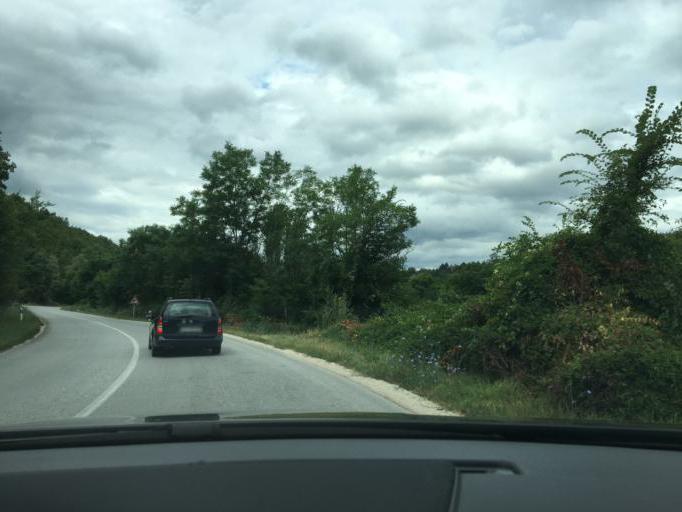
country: MK
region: Kratovo
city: Kratovo
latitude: 42.1749
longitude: 22.2227
